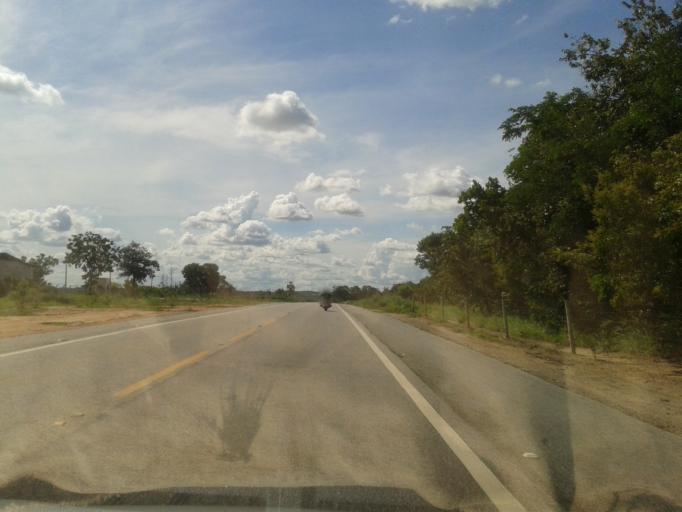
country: BR
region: Goias
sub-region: Itapirapua
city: Itapirapua
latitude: -15.2973
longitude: -50.4587
